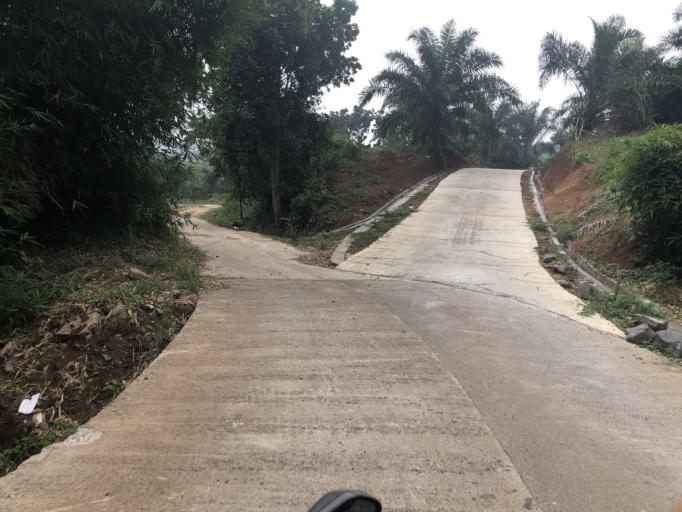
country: ID
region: West Java
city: Ciampea
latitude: -6.5493
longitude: 106.7155
